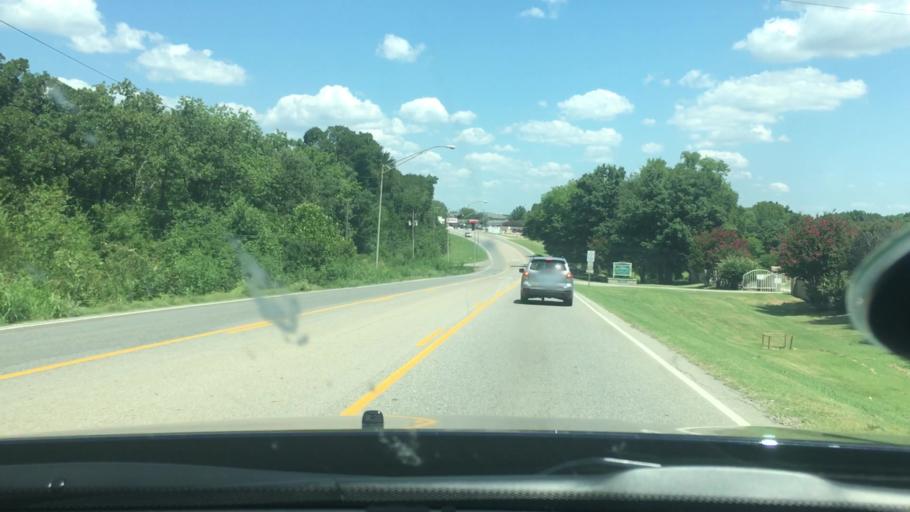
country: US
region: Oklahoma
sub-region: Marshall County
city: Madill
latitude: 34.0741
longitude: -96.7630
